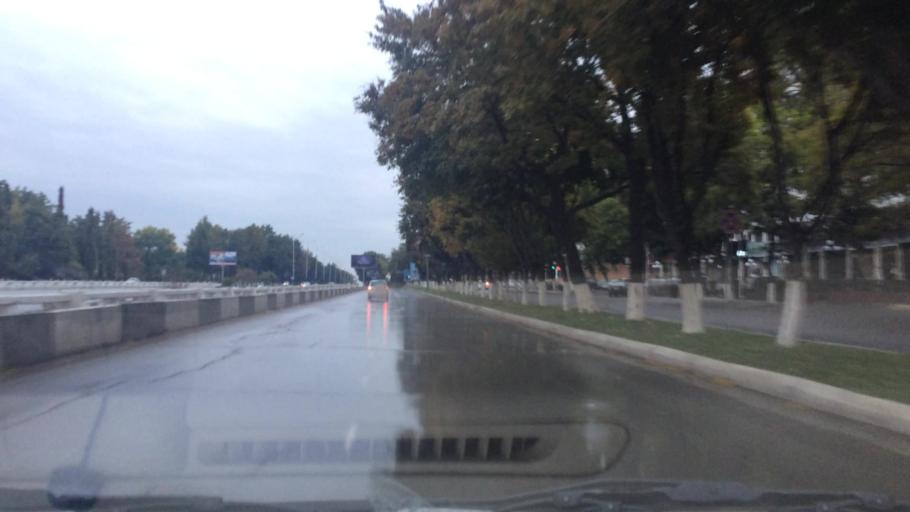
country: UZ
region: Toshkent Shahri
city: Tashkent
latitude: 41.3098
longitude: 69.2394
